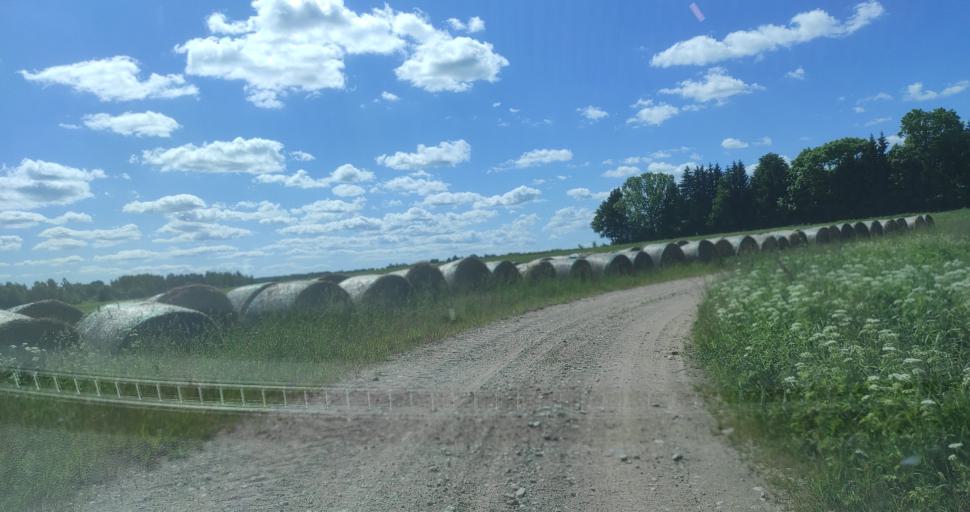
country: LV
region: Aizpute
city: Aizpute
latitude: 56.8599
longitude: 21.7076
